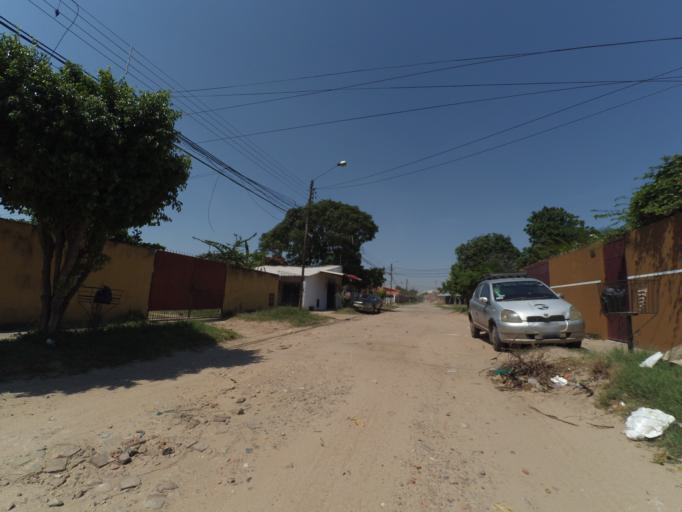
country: BO
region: Santa Cruz
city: Santa Cruz de la Sierra
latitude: -17.8208
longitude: -63.2244
